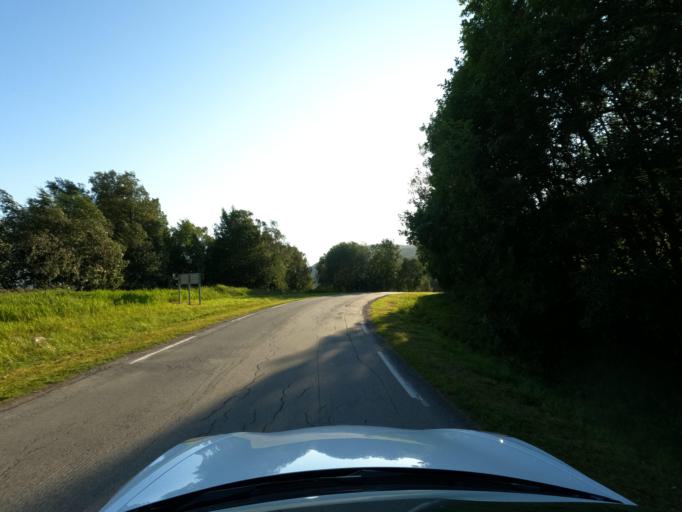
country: NO
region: Nordland
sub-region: Ballangen
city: Ballangen
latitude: 68.4680
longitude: 16.8045
